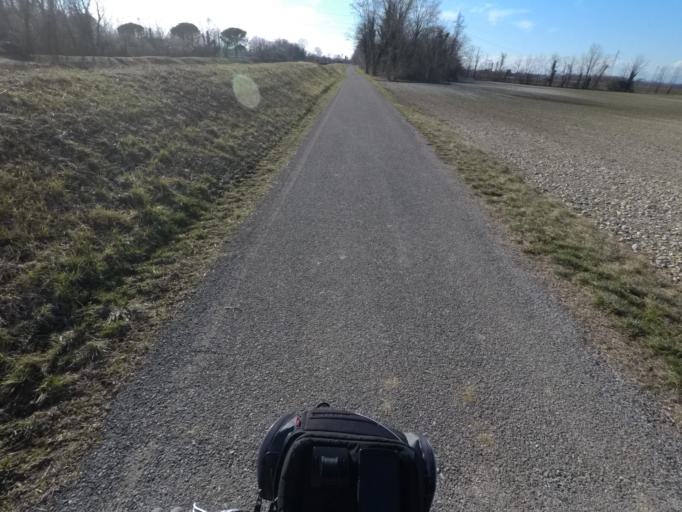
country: IT
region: Friuli Venezia Giulia
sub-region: Provincia di Udine
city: Moimacco
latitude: 46.0977
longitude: 13.3780
